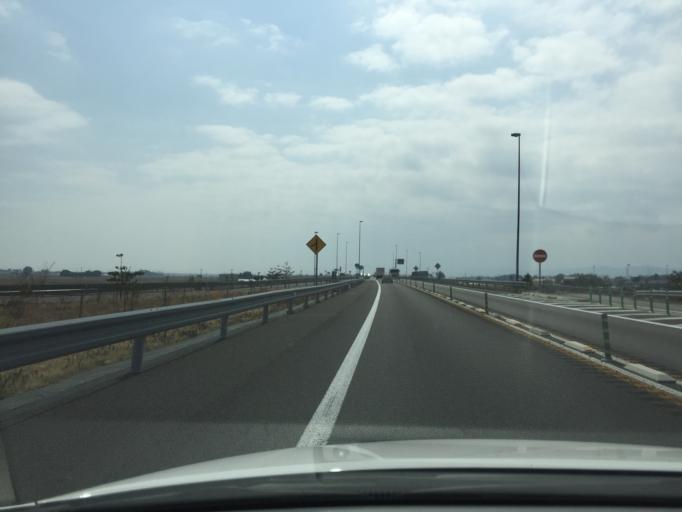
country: JP
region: Miyagi
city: Iwanuma
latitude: 38.0875
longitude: 140.8868
